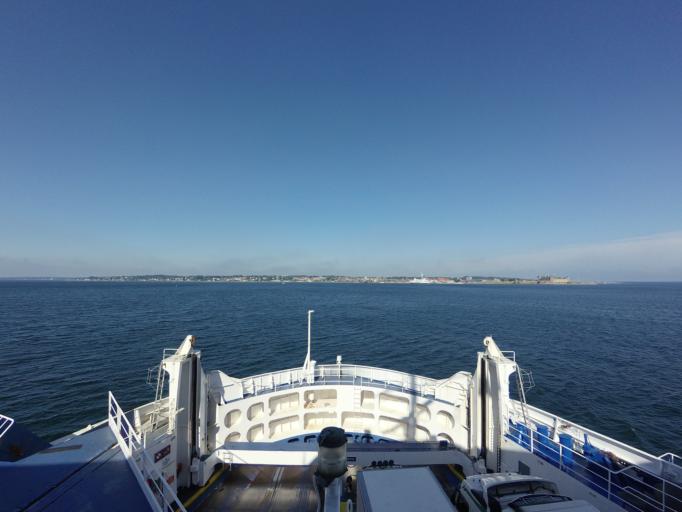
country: DK
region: Capital Region
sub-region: Helsingor Kommune
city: Helsingor
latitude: 56.0301
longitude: 12.6429
